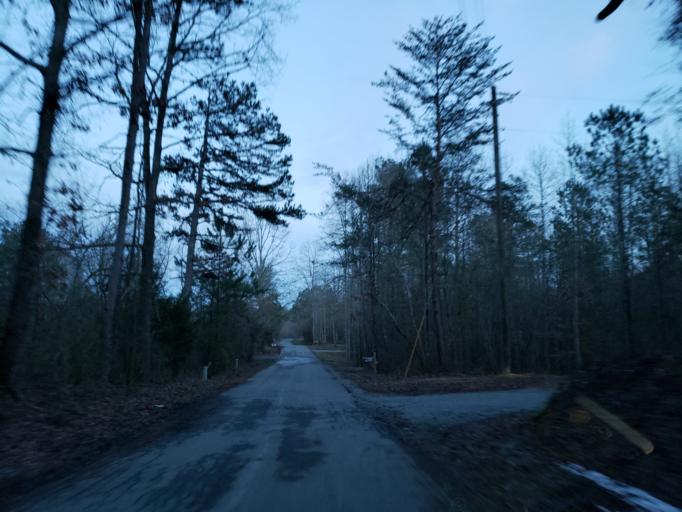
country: US
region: Georgia
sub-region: Cherokee County
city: Ball Ground
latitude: 34.2917
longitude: -84.2986
